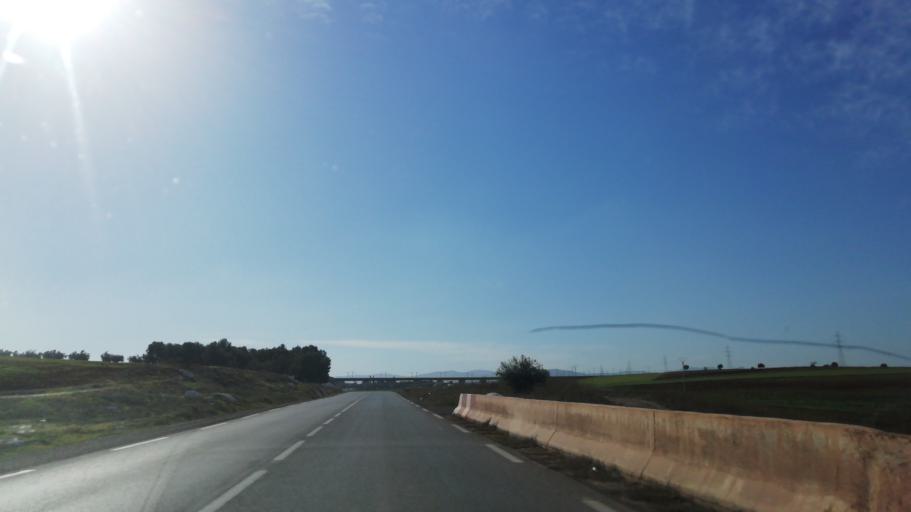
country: DZ
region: Tlemcen
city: Ouled Mimoun
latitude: 35.0143
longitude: -0.9053
